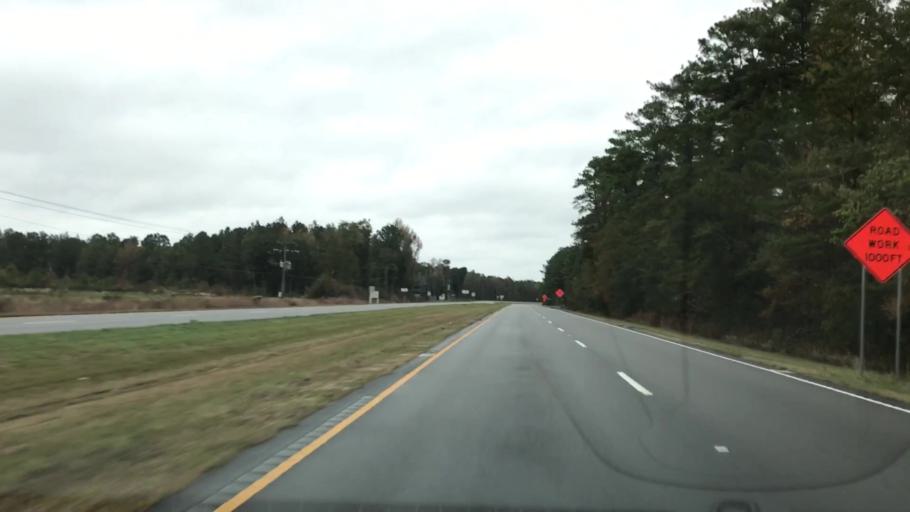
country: US
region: South Carolina
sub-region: Georgetown County
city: Georgetown
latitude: 33.2900
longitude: -79.3477
